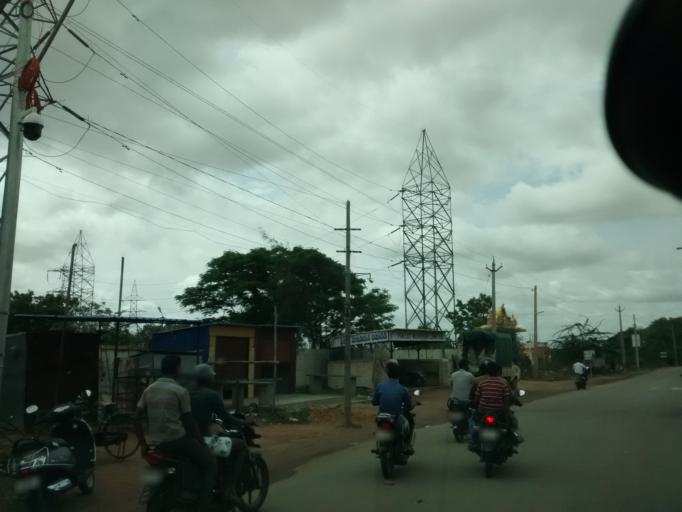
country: IN
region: Andhra Pradesh
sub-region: Anantapur
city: Hindupur
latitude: 13.8548
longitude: 77.4805
